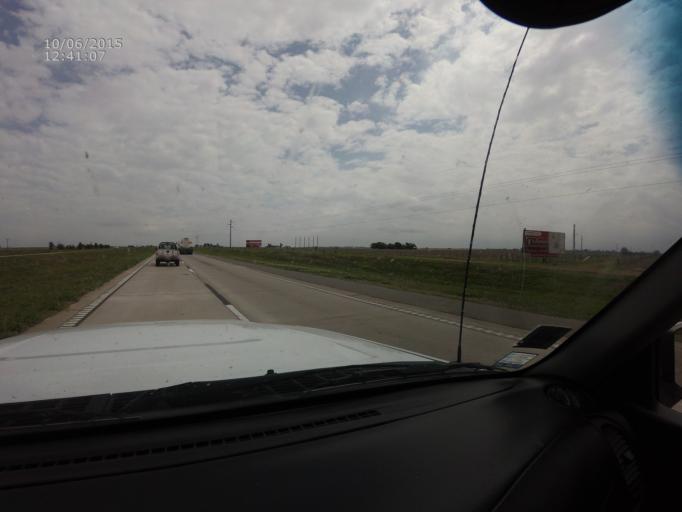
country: AR
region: Santa Fe
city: Canada de Gomez
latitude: -32.8623
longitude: -61.2983
